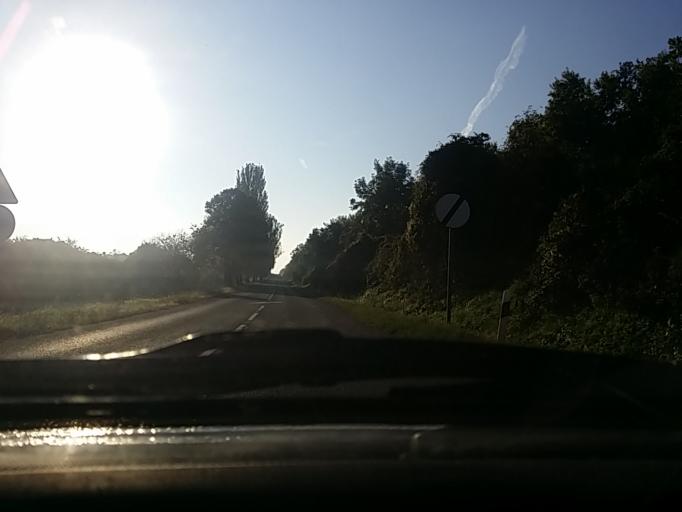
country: HU
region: Komarom-Esztergom
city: Pilismarot
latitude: 47.7983
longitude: 18.8593
